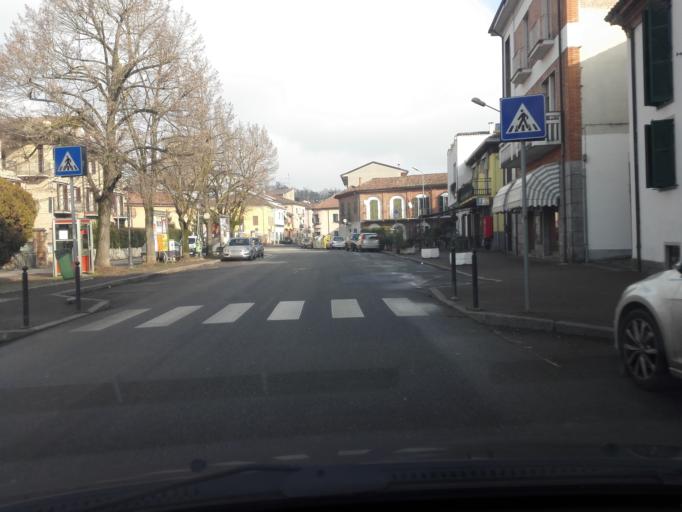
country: IT
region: Piedmont
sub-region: Provincia di Alessandria
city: Valle San Bartolomeo
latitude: 44.9554
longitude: 8.6432
